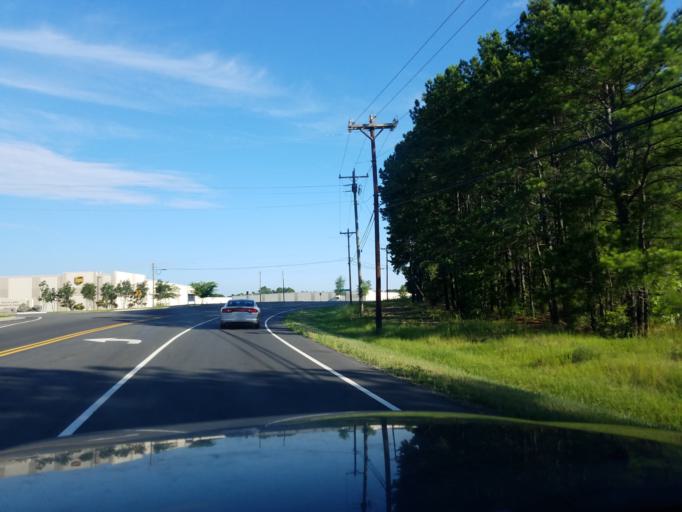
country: US
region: North Carolina
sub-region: Granville County
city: Butner
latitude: 36.1232
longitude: -78.7497
